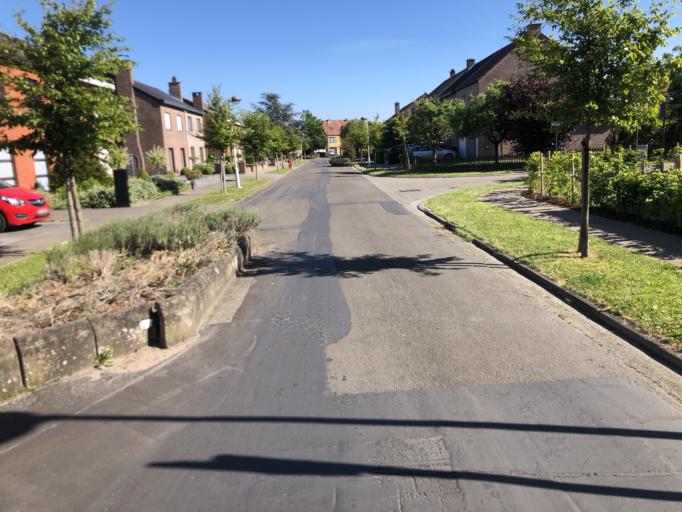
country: BE
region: Flanders
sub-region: Provincie Oost-Vlaanderen
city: Beveren
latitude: 51.2149
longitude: 4.2775
